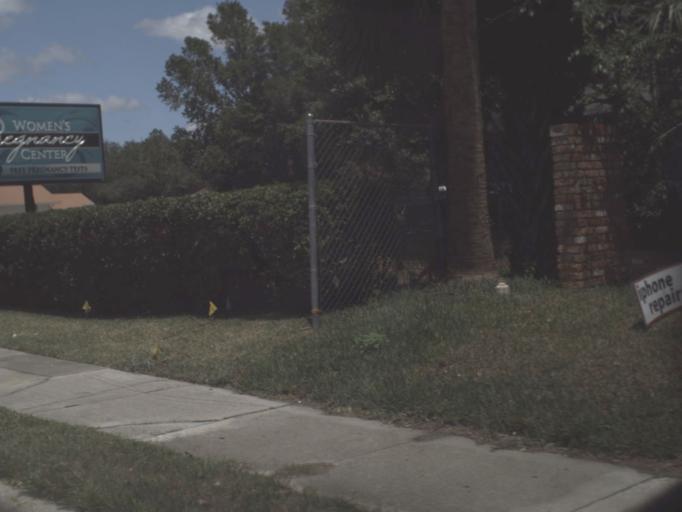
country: US
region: Florida
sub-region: Marion County
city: Ocala
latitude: 29.1870
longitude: -82.1149
